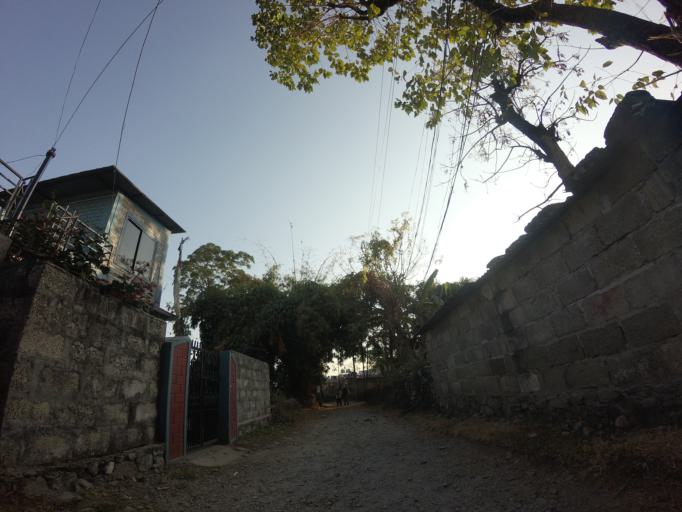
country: NP
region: Western Region
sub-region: Gandaki Zone
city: Pokhara
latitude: 28.2087
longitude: 83.9961
